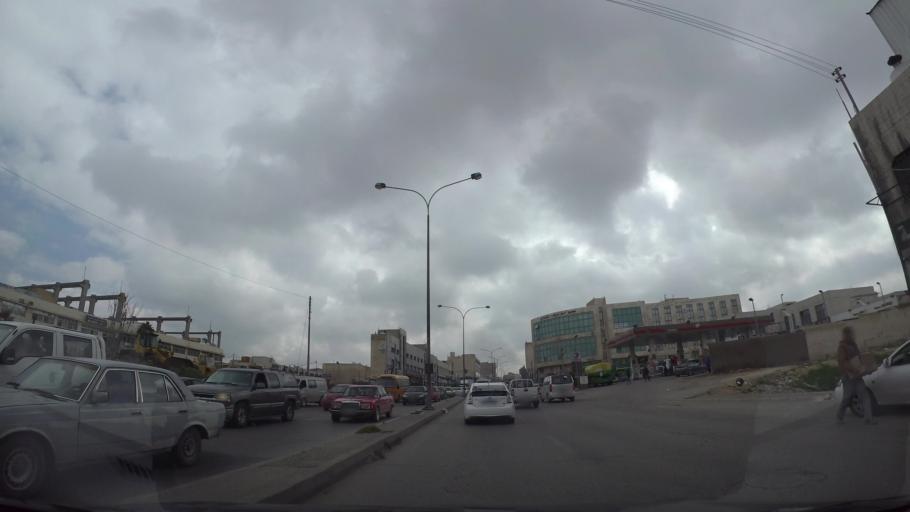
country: JO
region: Amman
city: Al Quwaysimah
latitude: 31.9127
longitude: 35.9389
